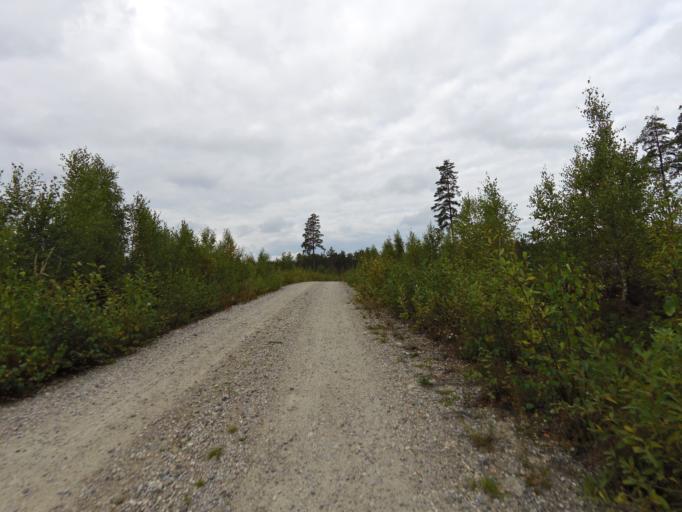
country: SE
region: Gaevleborg
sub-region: Gavle Kommun
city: Valbo
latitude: 60.7306
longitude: 17.0307
